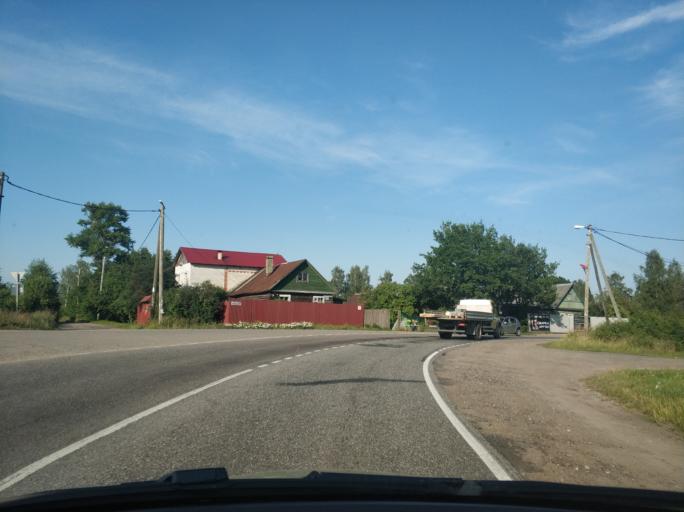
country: RU
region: Leningrad
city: Borisova Griva
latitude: 60.0955
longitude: 30.9678
